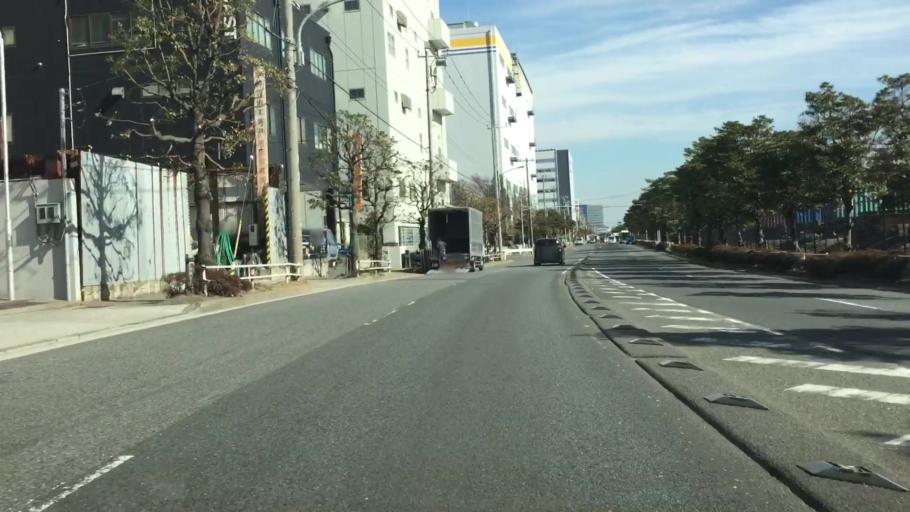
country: JP
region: Tokyo
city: Urayasu
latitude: 35.6419
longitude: 139.8100
